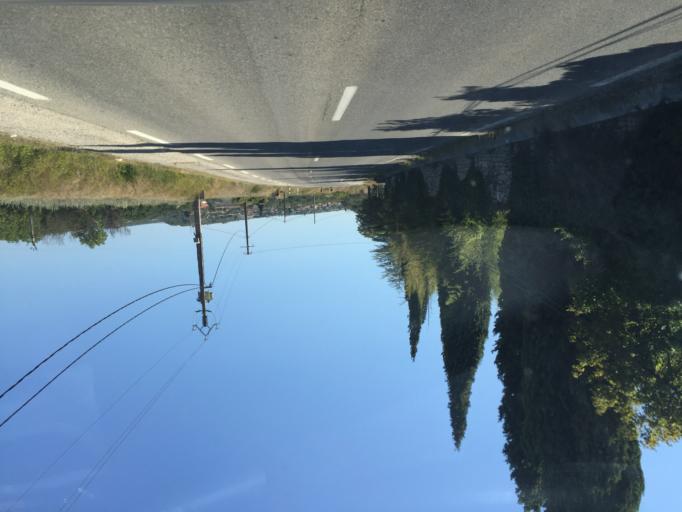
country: FR
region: Provence-Alpes-Cote d'Azur
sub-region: Departement des Alpes-de-Haute-Provence
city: Forcalquier
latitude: 43.9583
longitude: 5.7983
